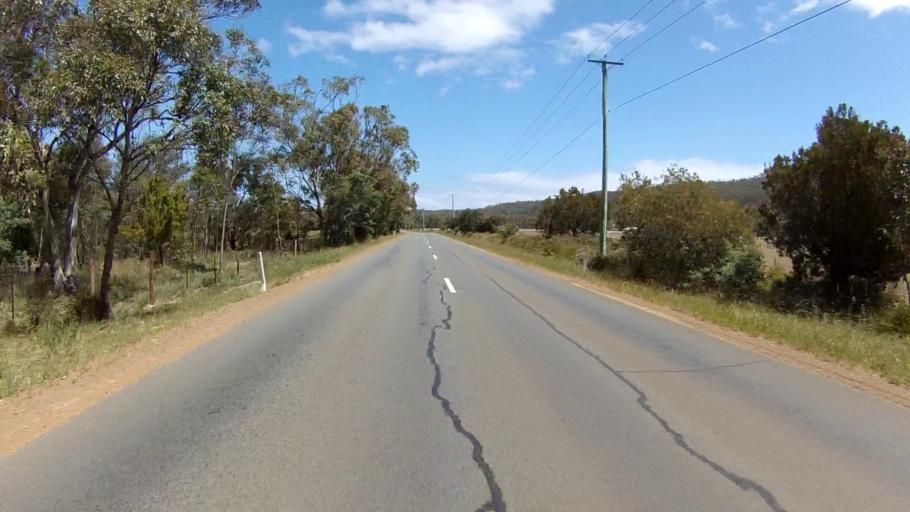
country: AU
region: Tasmania
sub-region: Clarence
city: Sandford
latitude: -42.9426
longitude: 147.4862
